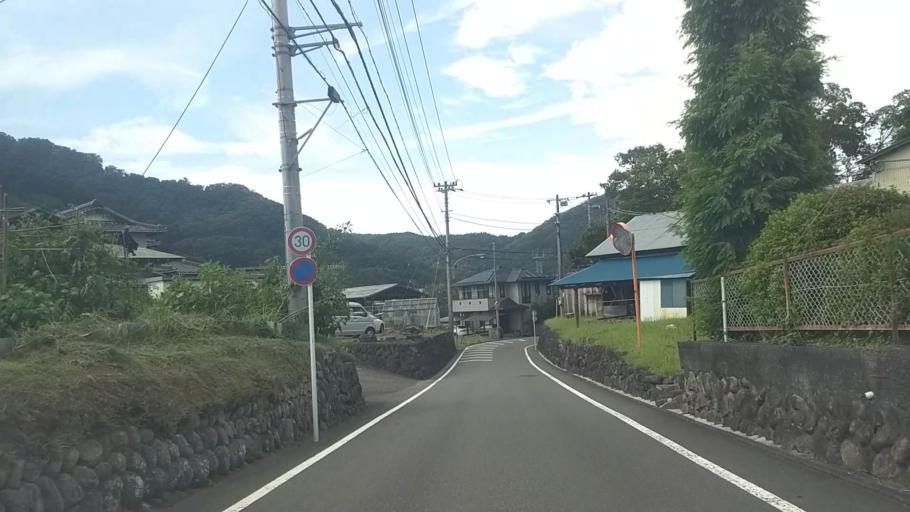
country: JP
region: Shizuoka
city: Ito
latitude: 34.9736
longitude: 138.9494
